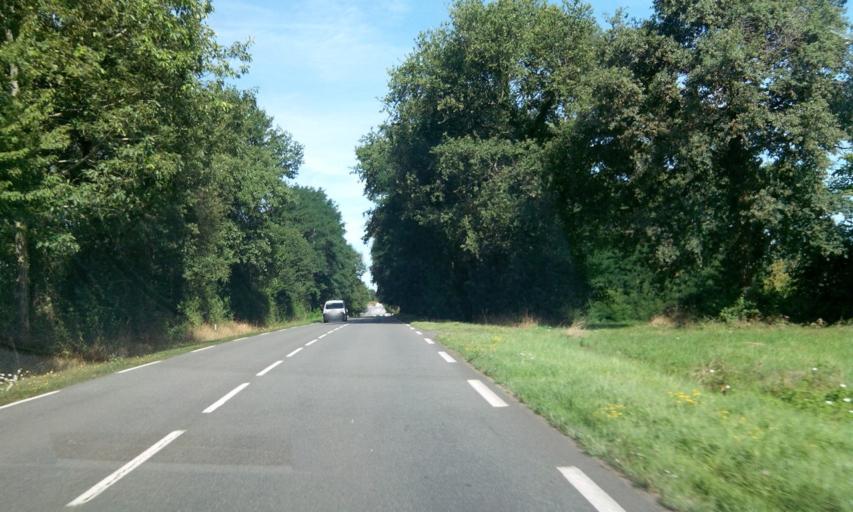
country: FR
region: Poitou-Charentes
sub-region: Departement de la Charente
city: Confolens
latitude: 45.9559
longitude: 0.7063
